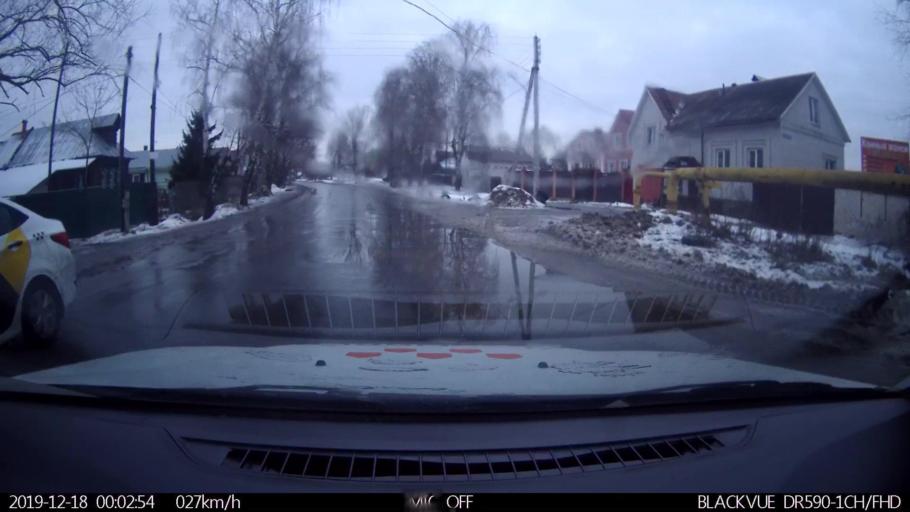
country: RU
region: Nizjnij Novgorod
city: Gorbatovka
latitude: 56.3651
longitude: 43.8321
